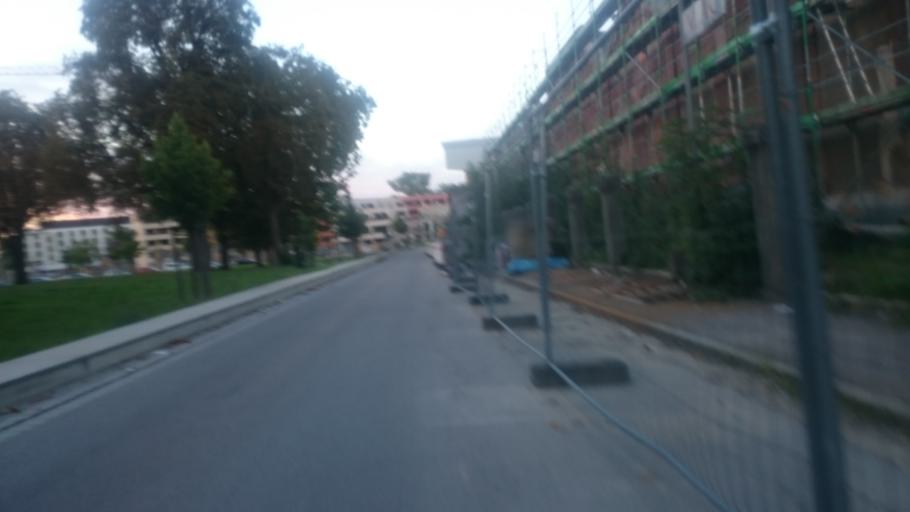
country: DE
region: Bavaria
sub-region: Swabia
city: Augsburg
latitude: 48.3629
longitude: 10.9121
